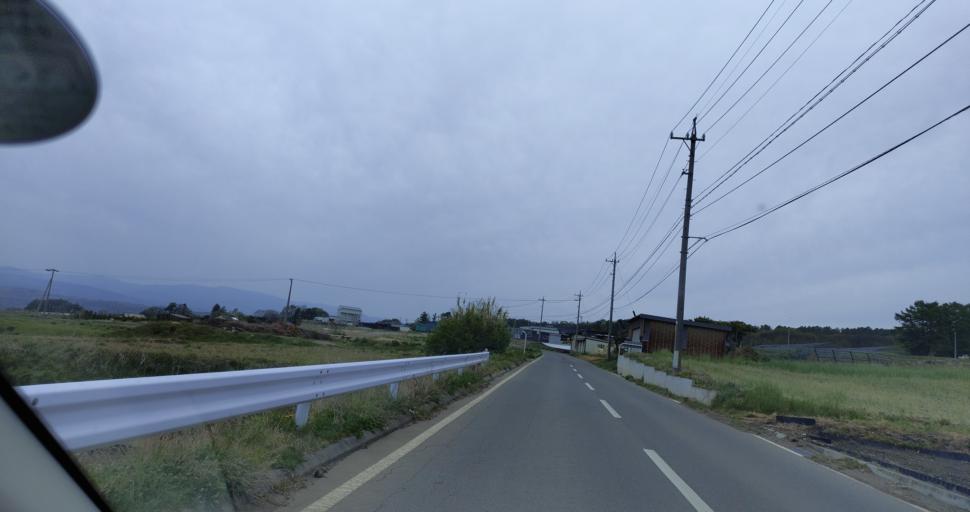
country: JP
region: Nagano
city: Komoro
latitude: 36.3369
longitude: 138.4789
